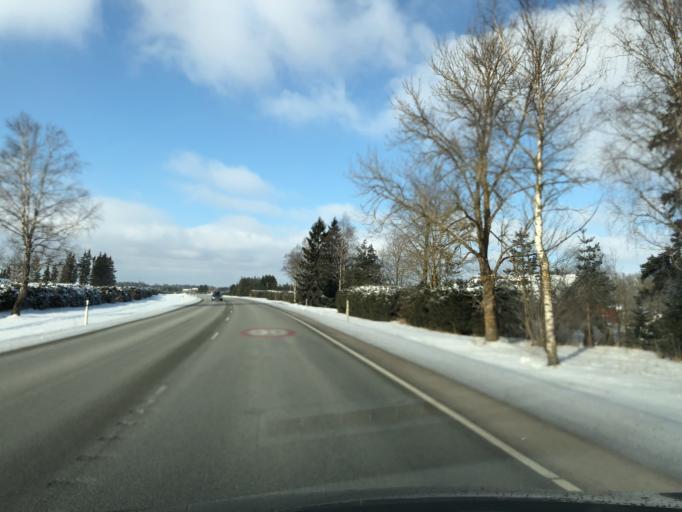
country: EE
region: Jaervamaa
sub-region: Paide linn
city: Paide
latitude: 58.8465
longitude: 25.7349
